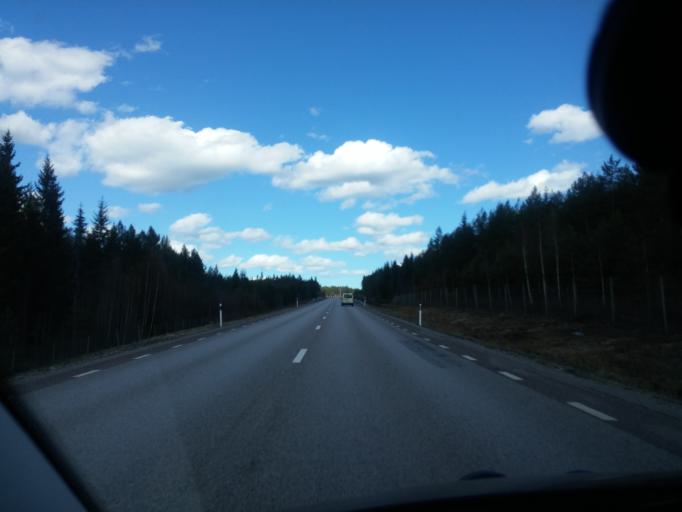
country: SE
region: Dalarna
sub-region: Faluns Kommun
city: Falun
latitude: 60.6605
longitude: 15.6461
